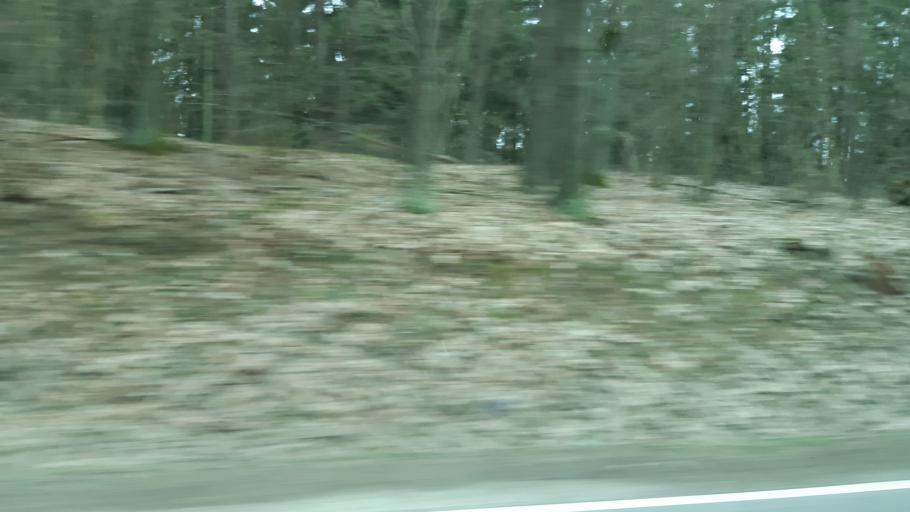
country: PL
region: Podlasie
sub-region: Suwalki
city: Suwalki
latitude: 54.3099
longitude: 22.9573
